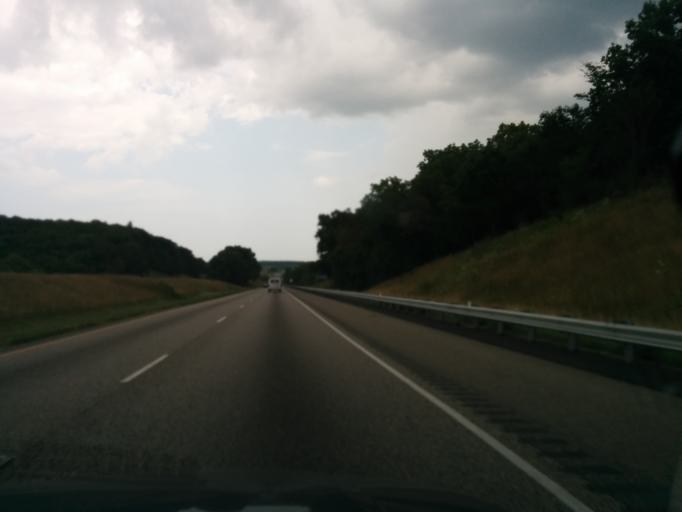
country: US
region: Virginia
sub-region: Augusta County
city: Verona
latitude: 38.1503
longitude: -79.0169
